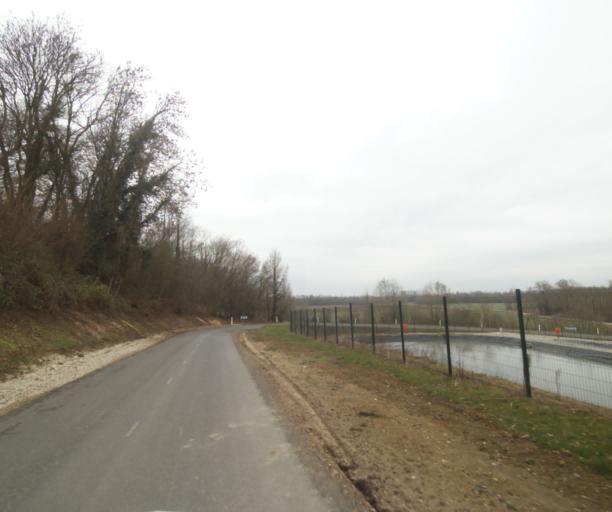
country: FR
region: Champagne-Ardenne
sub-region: Departement de la Haute-Marne
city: Villiers-en-Lieu
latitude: 48.6360
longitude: 4.8360
